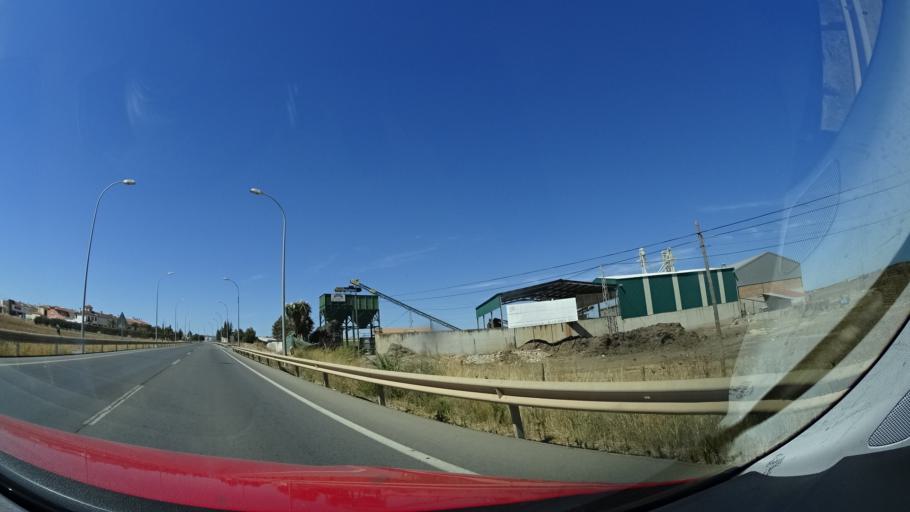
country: ES
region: Andalusia
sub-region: Provincia de Malaga
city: Campillos
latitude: 37.0504
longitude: -4.8538
